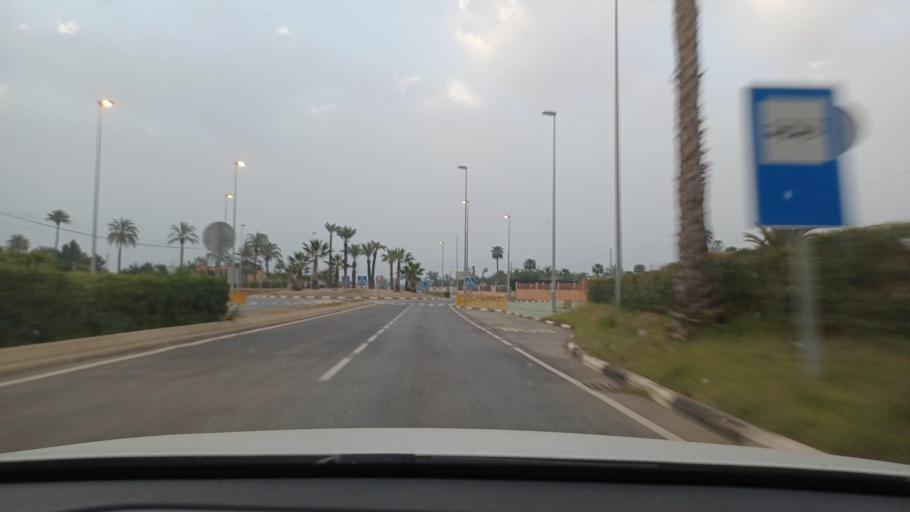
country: ES
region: Valencia
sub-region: Provincia de Alicante
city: Elche
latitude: 38.2226
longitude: -0.6980
